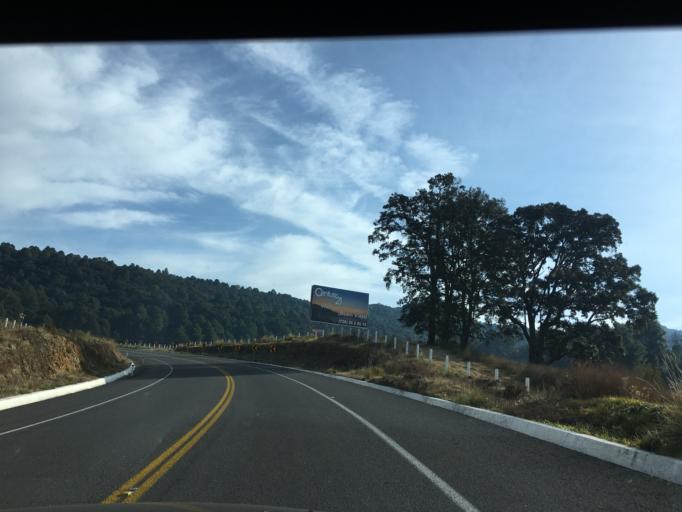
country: MX
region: Mexico
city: San Bartolo
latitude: 19.2721
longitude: -100.0575
